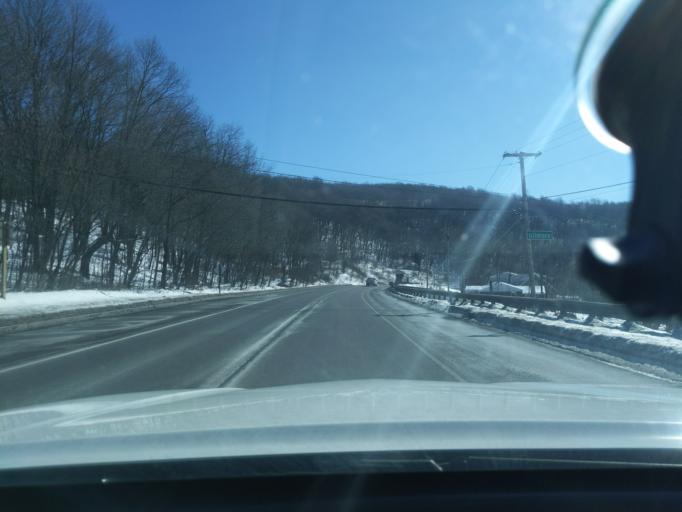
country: US
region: Maryland
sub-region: Allegany County
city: Lonaconing
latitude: 39.5876
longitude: -78.9507
